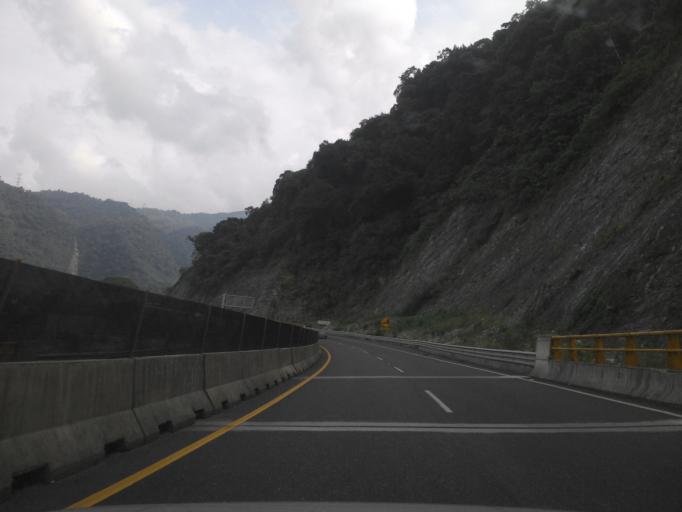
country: MX
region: Puebla
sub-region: Xicotepec
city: San Lorenzo
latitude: 20.3539
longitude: -97.9635
